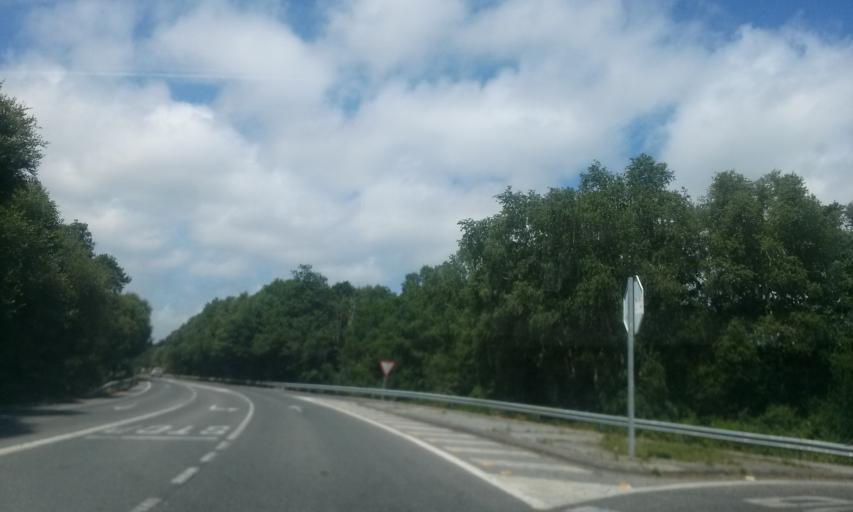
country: ES
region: Galicia
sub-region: Provincia de Lugo
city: Friol
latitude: 43.0352
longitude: -7.7167
